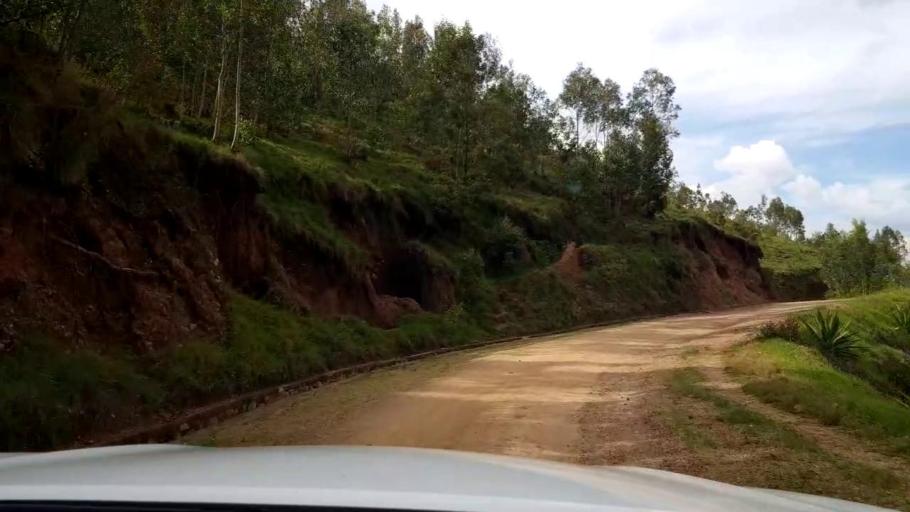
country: RW
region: Southern Province
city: Gitarama
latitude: -1.9952
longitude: 29.7081
